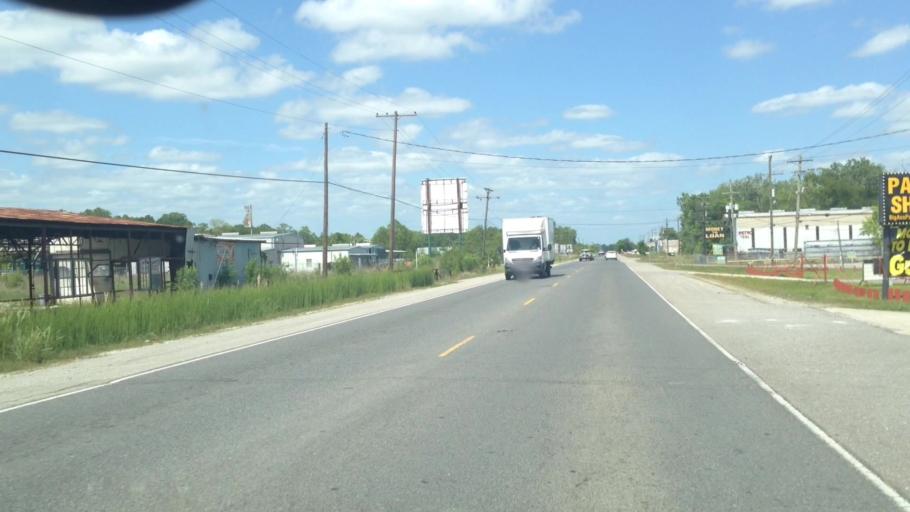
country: US
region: Louisiana
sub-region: Terrebonne Parish
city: Houma
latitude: 29.6482
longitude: -90.6852
